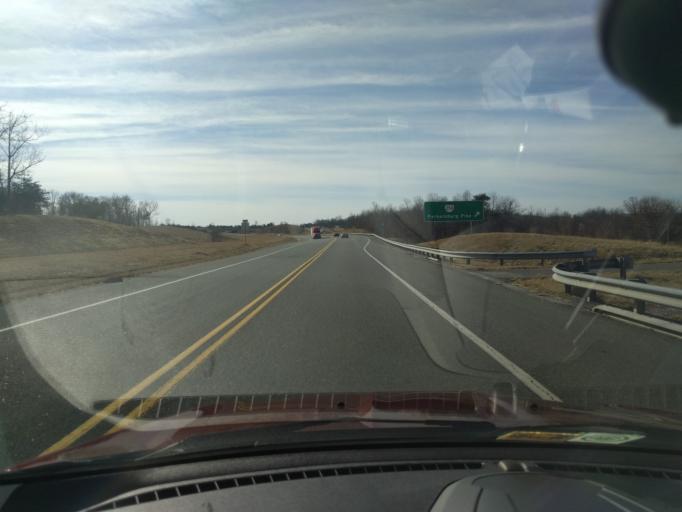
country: US
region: Virginia
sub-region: City of Staunton
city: Staunton
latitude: 38.1567
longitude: -79.1143
